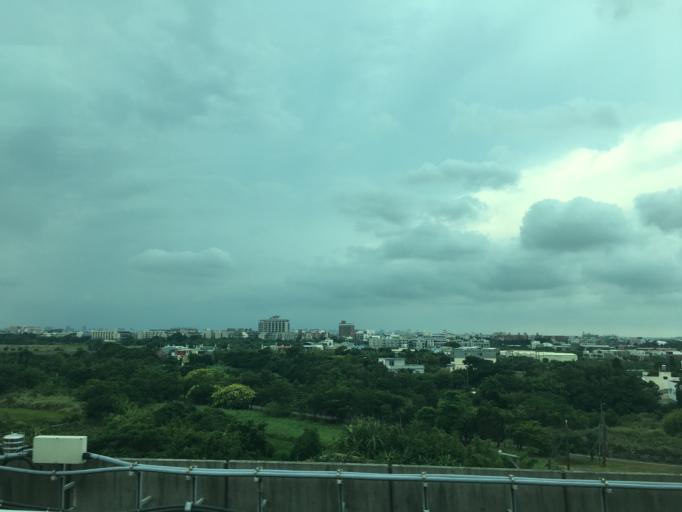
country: TW
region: Taiwan
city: Taoyuan City
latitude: 25.0870
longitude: 121.2652
